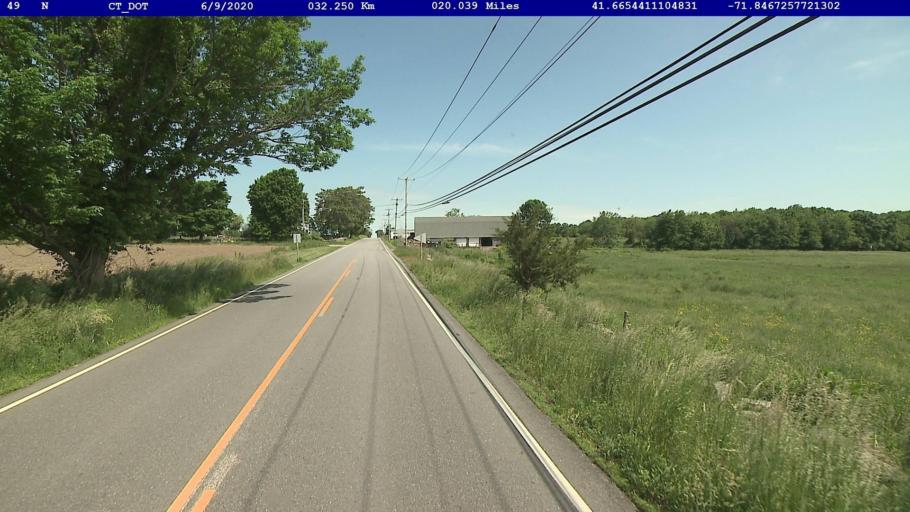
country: US
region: Connecticut
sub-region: Windham County
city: Moosup
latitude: 41.6655
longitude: -71.8468
